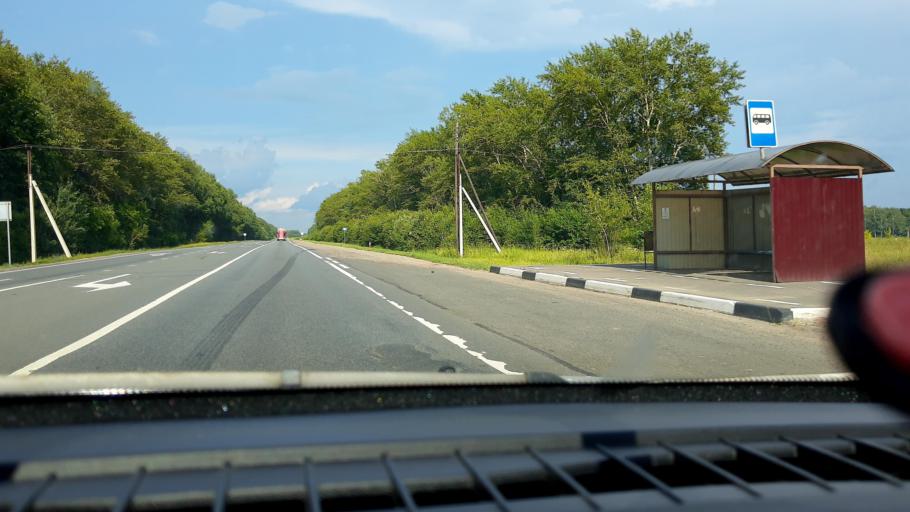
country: RU
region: Nizjnij Novgorod
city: Pervoye Maya
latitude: 55.9923
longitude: 44.7844
